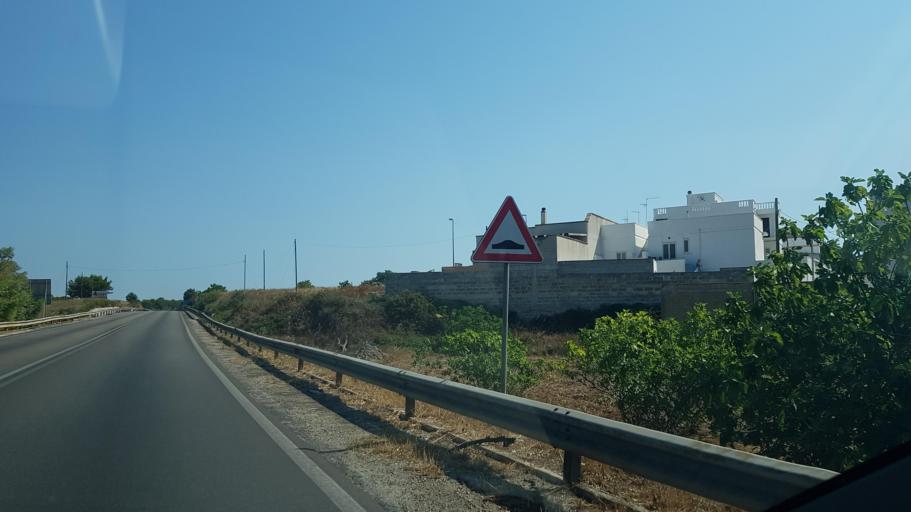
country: IT
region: Apulia
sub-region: Provincia di Lecce
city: Nociglia
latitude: 40.0405
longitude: 18.3213
